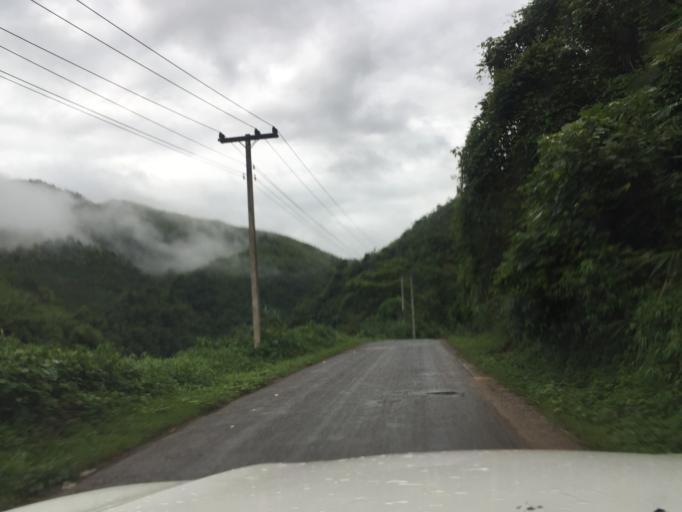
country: LA
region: Oudomxai
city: Muang La
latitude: 20.9429
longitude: 102.2074
